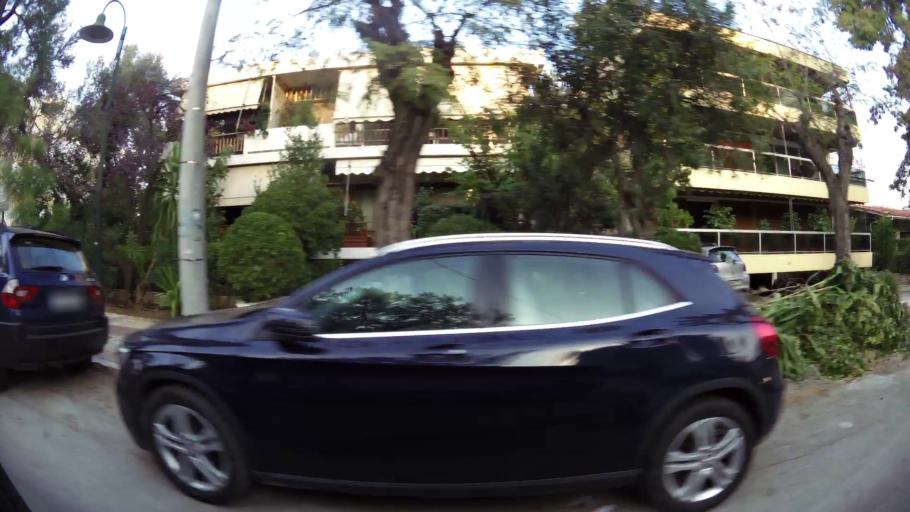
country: GR
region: Attica
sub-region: Nomarchia Athinas
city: Psychiko
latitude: 38.0122
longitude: 23.7725
